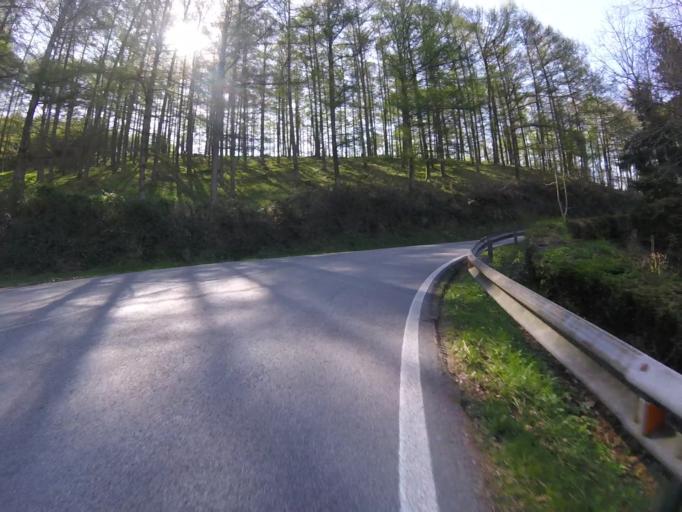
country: ES
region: Navarre
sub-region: Provincia de Navarra
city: Leitza
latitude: 43.0901
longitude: -1.8879
